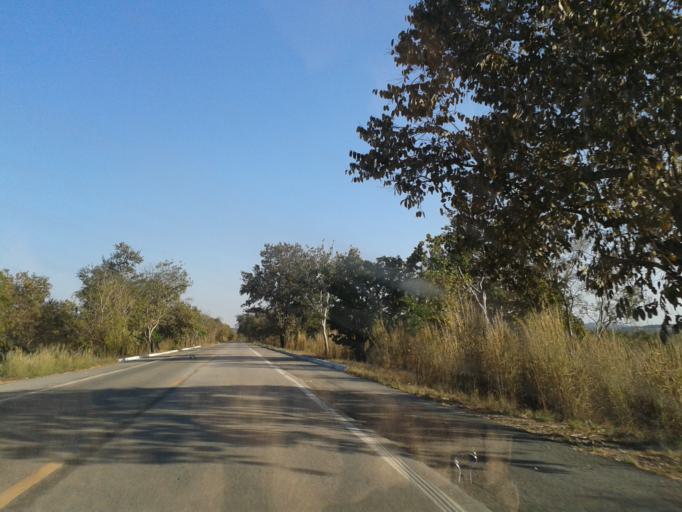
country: BR
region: Goias
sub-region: Itapuranga
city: Itapuranga
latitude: -15.3577
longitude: -50.3989
